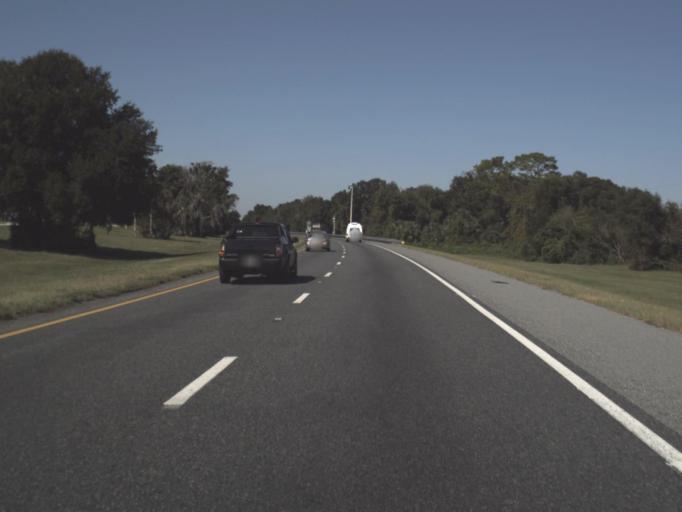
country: US
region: Florida
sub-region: Sumter County
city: Wildwood
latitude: 28.7865
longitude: -81.9796
